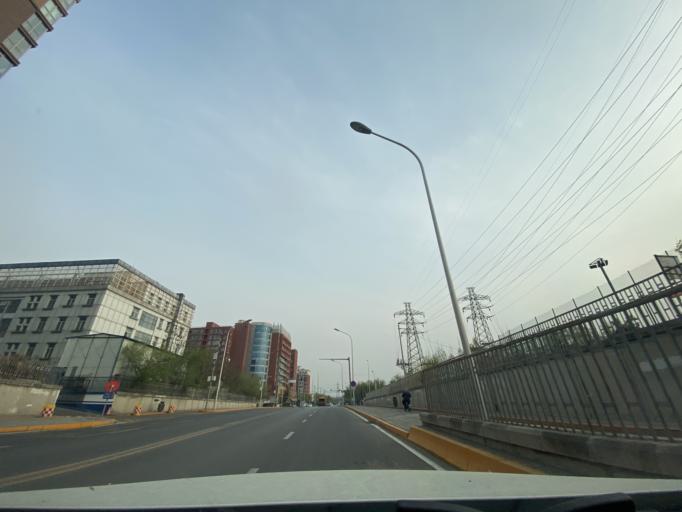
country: CN
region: Beijing
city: Babaoshan
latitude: 39.9293
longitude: 116.2328
